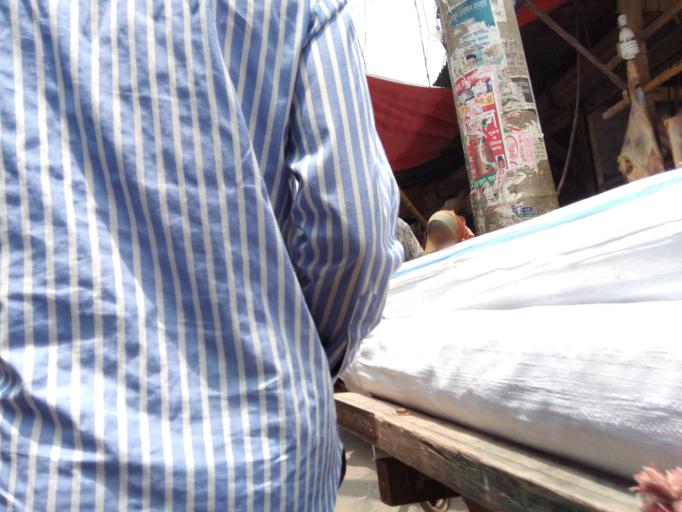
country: BD
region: Dhaka
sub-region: Dhaka
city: Dhaka
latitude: 23.7158
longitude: 90.3987
